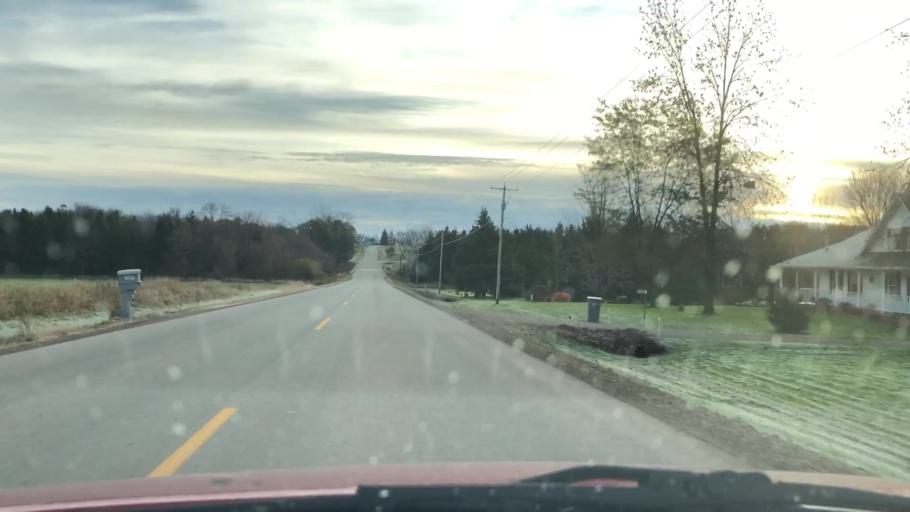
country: US
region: Wisconsin
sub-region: Brown County
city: Oneida
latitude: 44.4148
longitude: -88.2640
